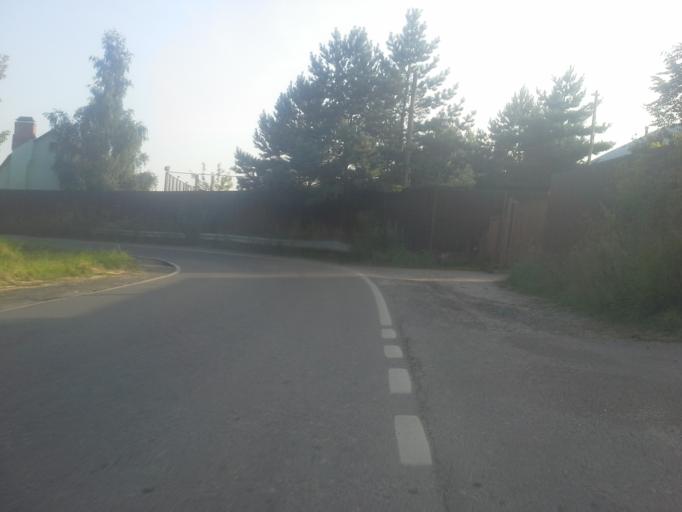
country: RU
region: Moskovskaya
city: Nikolina Gora
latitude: 55.7520
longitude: 36.9778
